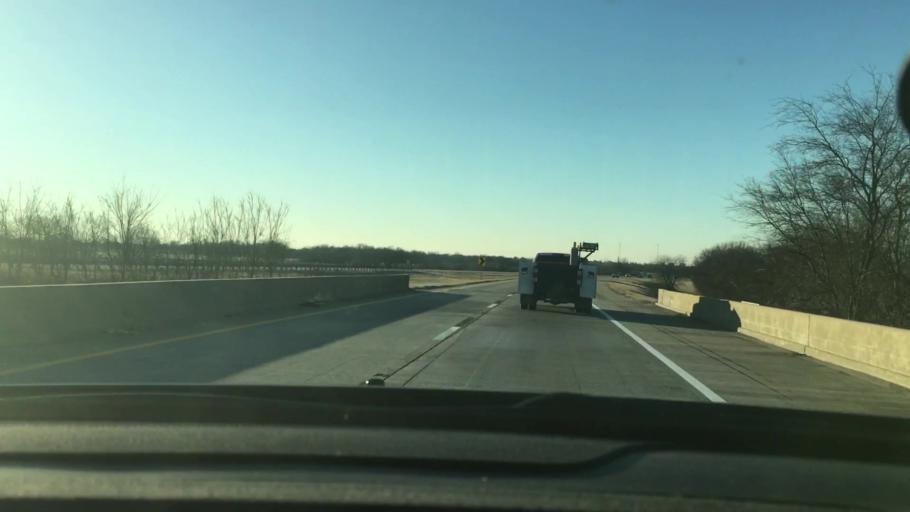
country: US
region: Oklahoma
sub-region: Murray County
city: Davis
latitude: 34.3474
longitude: -97.1480
